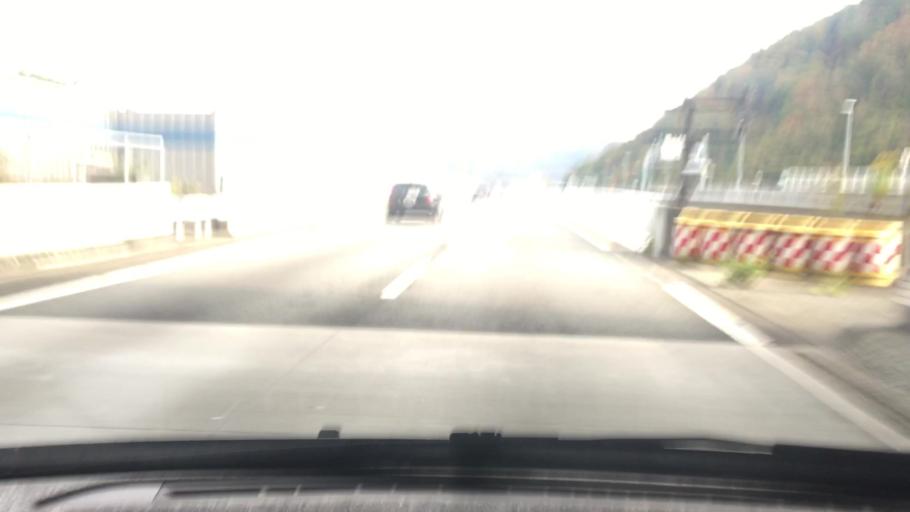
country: JP
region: Hyogo
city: Sandacho
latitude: 34.7870
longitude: 135.2153
